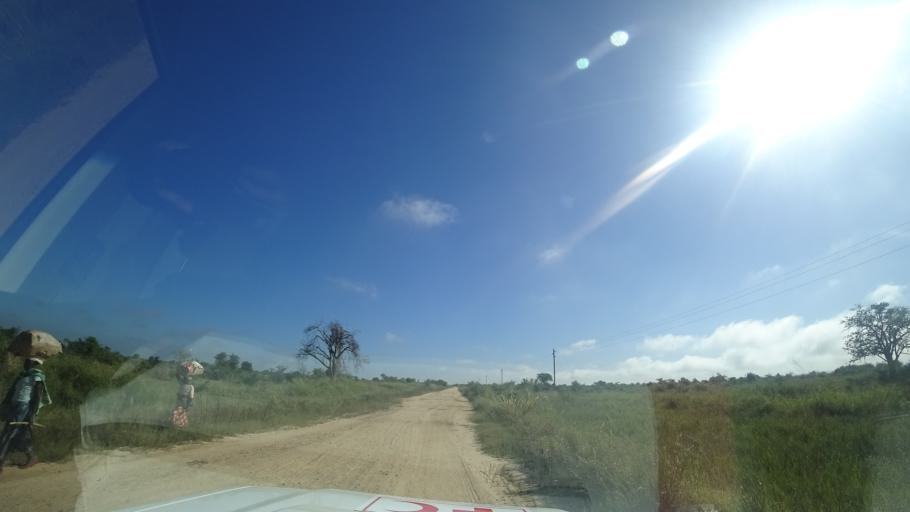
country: MZ
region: Sofala
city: Dondo
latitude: -19.4344
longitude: 34.5611
